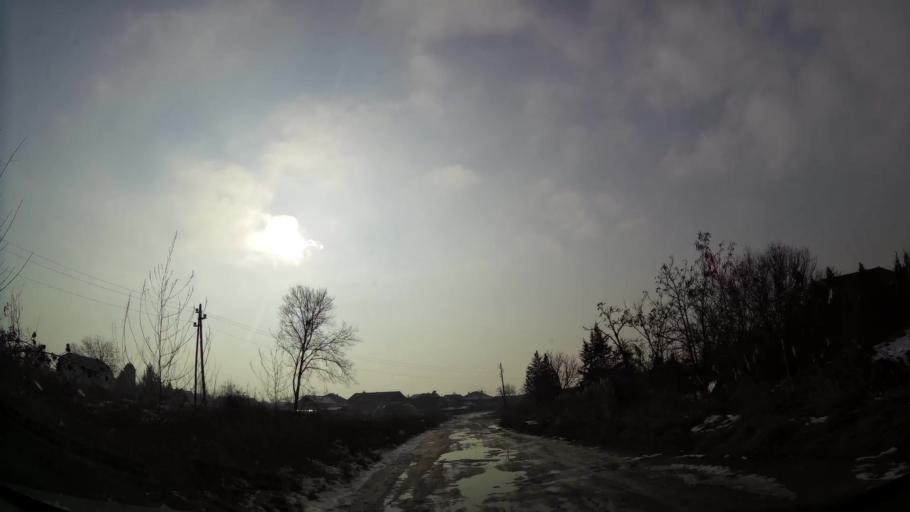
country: MK
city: Kadino
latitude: 41.9697
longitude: 21.6030
